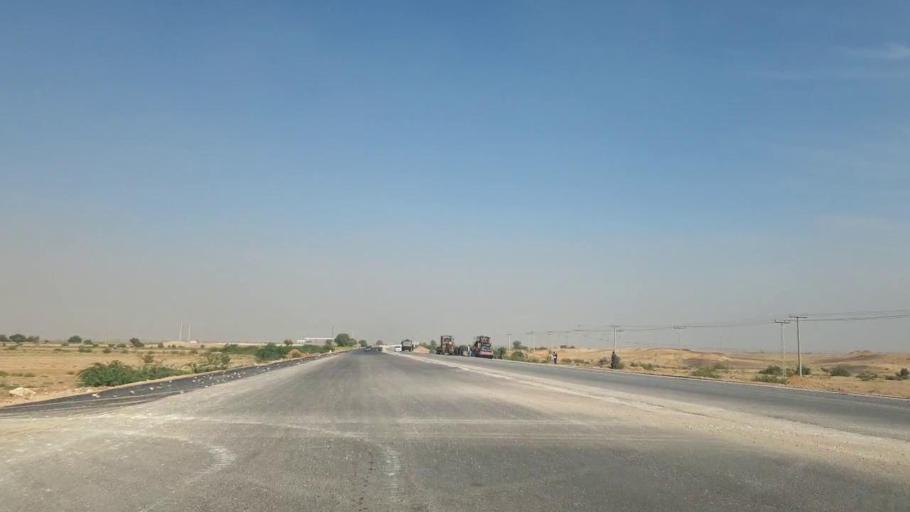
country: PK
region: Sindh
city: Jamshoro
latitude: 25.5295
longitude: 68.2801
